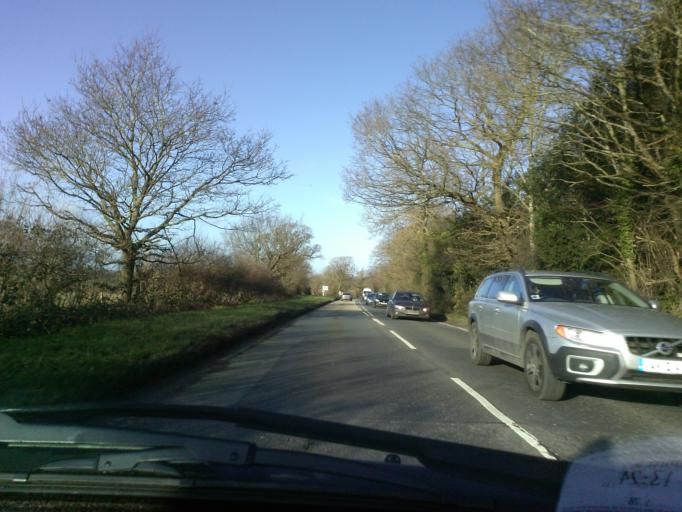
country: GB
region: England
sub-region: Hampshire
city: Romsey
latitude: 50.9635
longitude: -1.4756
